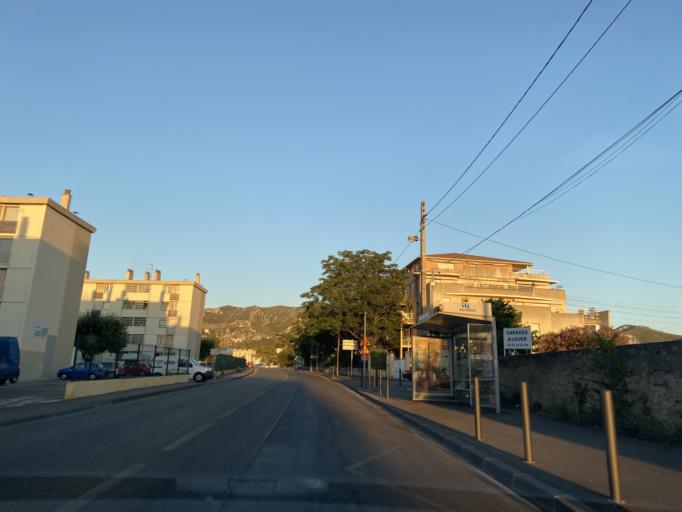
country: FR
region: Provence-Alpes-Cote d'Azur
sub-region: Departement des Bouches-du-Rhone
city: Marseille 10
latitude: 43.2761
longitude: 5.4225
